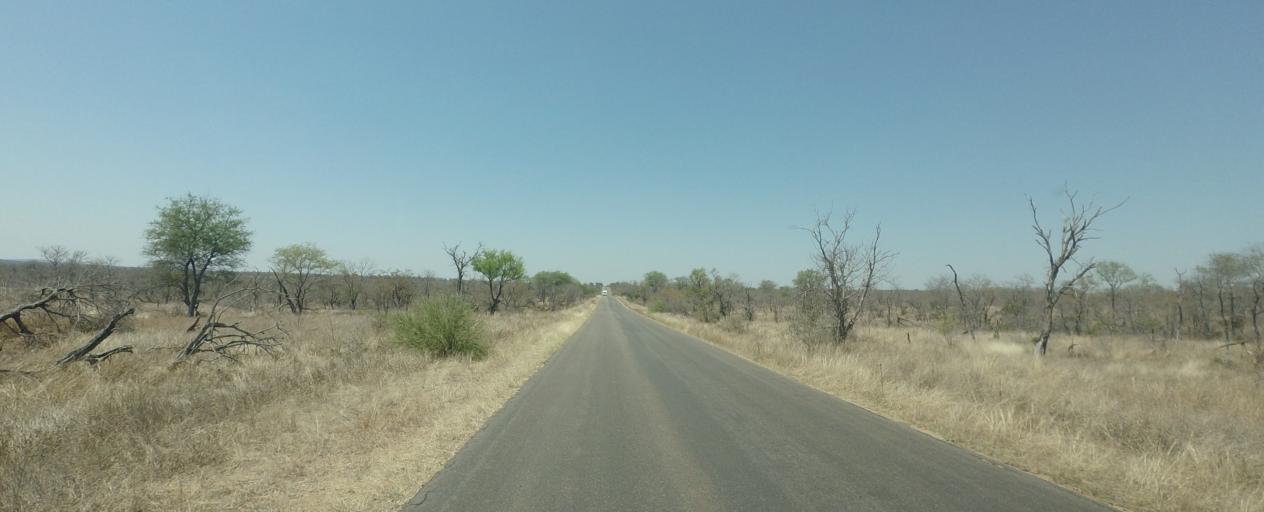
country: ZA
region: Limpopo
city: Thulamahashi
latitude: -24.4731
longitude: 31.4116
